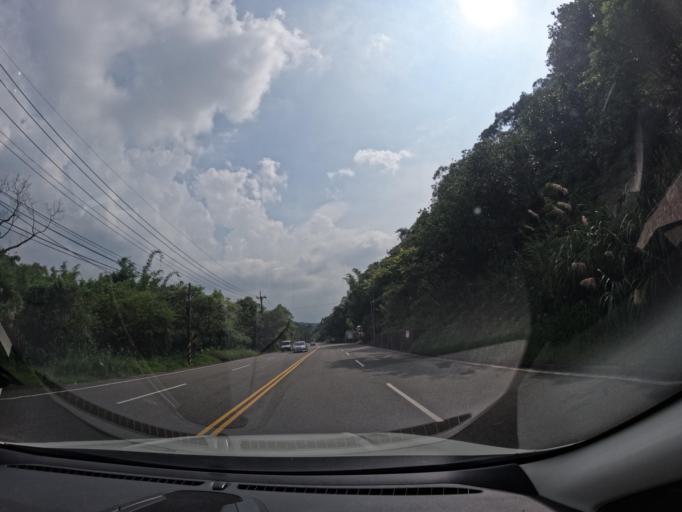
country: TW
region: Taiwan
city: Daxi
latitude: 24.8951
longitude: 121.3309
